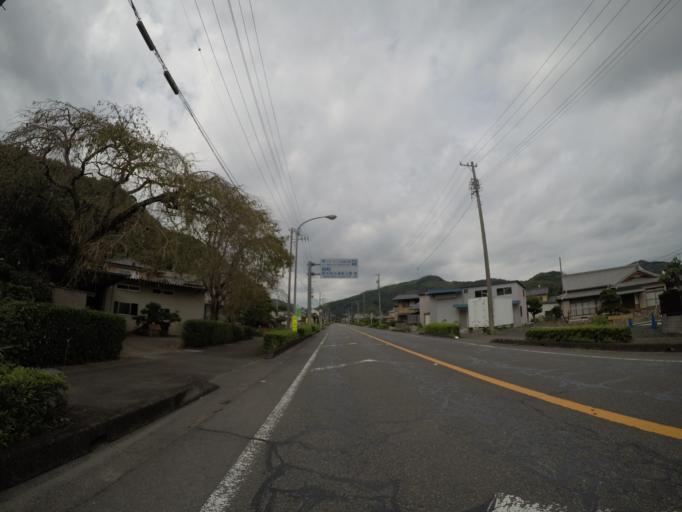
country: JP
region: Shizuoka
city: Fujieda
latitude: 34.8735
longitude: 138.2260
